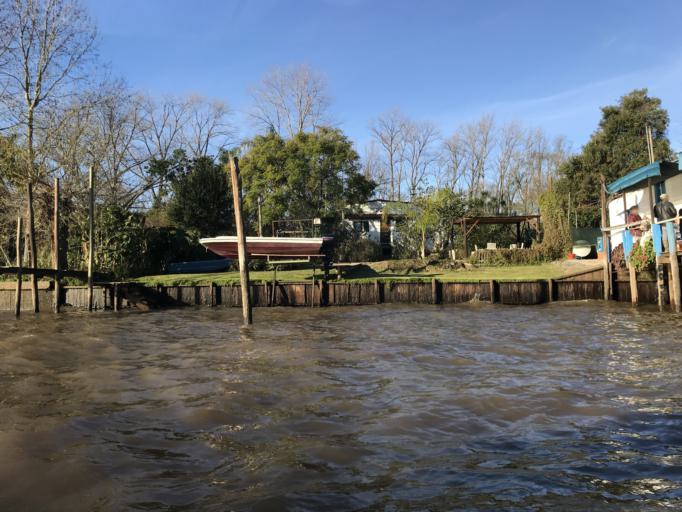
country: AR
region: Buenos Aires
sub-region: Partido de Tigre
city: Tigre
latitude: -34.4021
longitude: -58.5943
